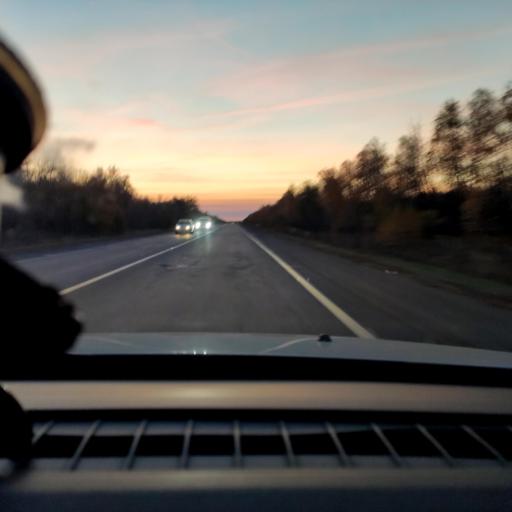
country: RU
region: Samara
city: Chapayevsk
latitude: 52.9895
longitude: 49.8494
